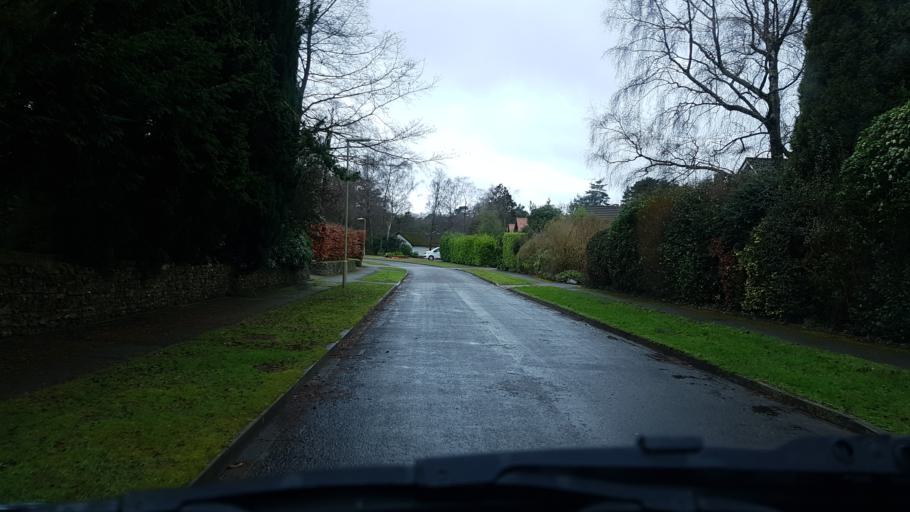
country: GB
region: England
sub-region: Surrey
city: Hindhead
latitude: 51.1070
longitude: -0.7552
